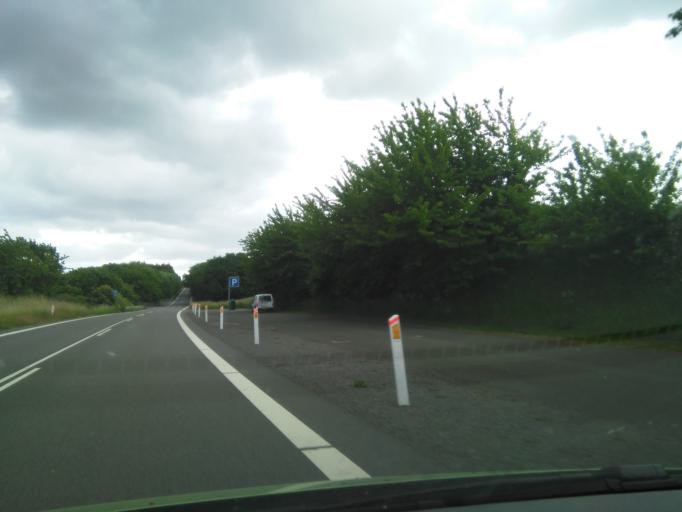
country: DK
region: Capital Region
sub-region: Bornholm Kommune
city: Akirkeby
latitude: 55.2155
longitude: 14.9269
